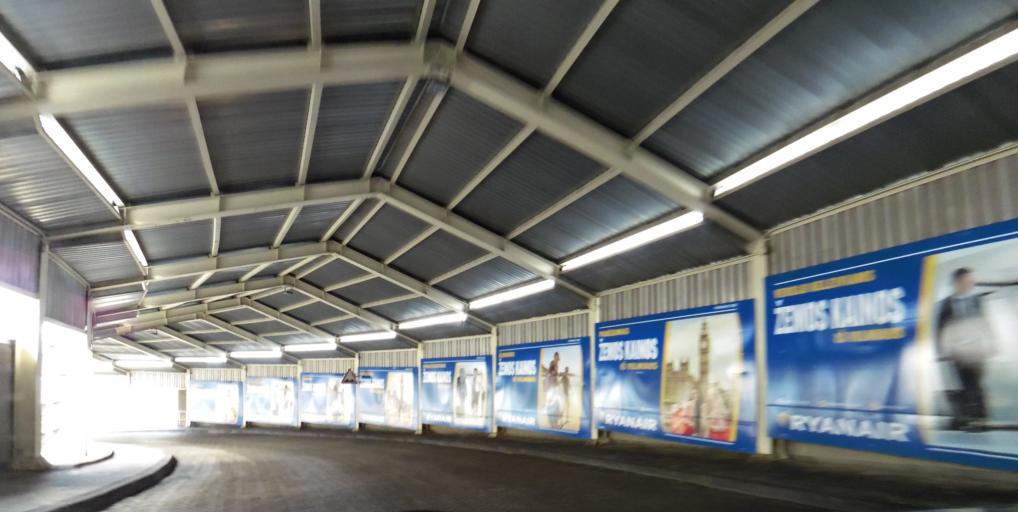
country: LT
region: Vilnius County
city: Naujamiestis
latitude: 54.6433
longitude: 25.2802
